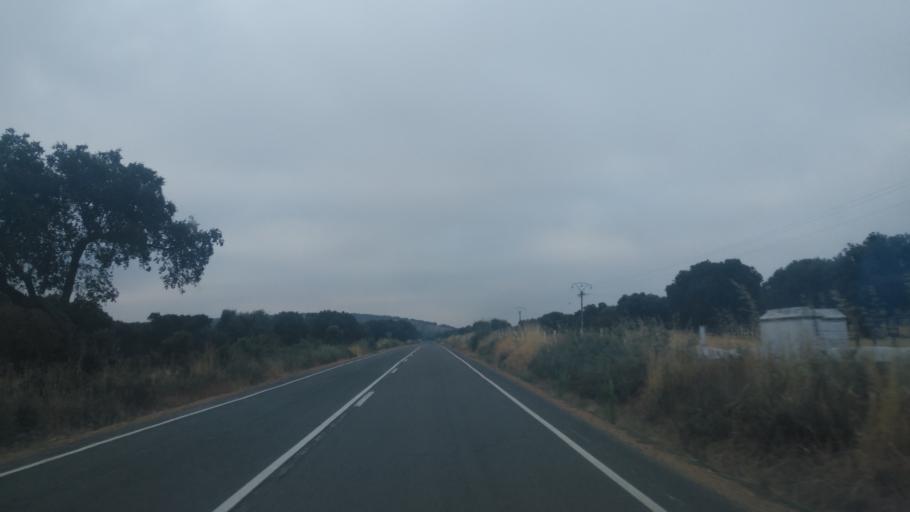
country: ES
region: Castille and Leon
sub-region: Provincia de Salamanca
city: Matilla de los Canos del Rio
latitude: 40.8108
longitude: -5.9306
